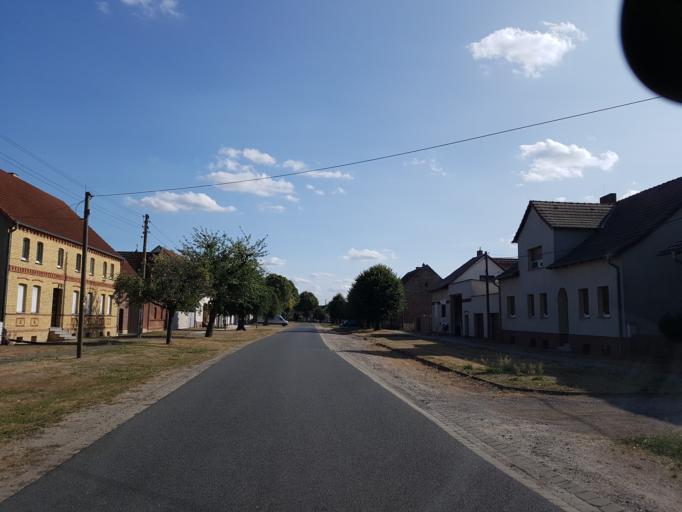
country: DE
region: Brandenburg
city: Juterbog
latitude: 51.8964
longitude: 13.1136
